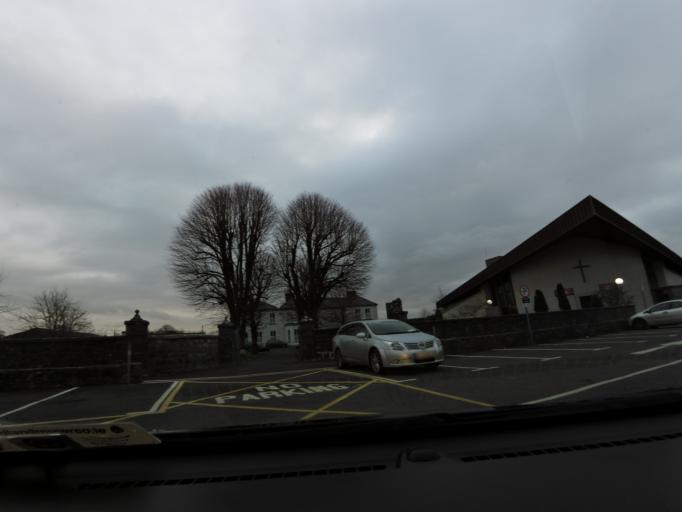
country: IE
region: Connaught
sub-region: County Galway
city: Athenry
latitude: 53.3001
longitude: -8.7494
